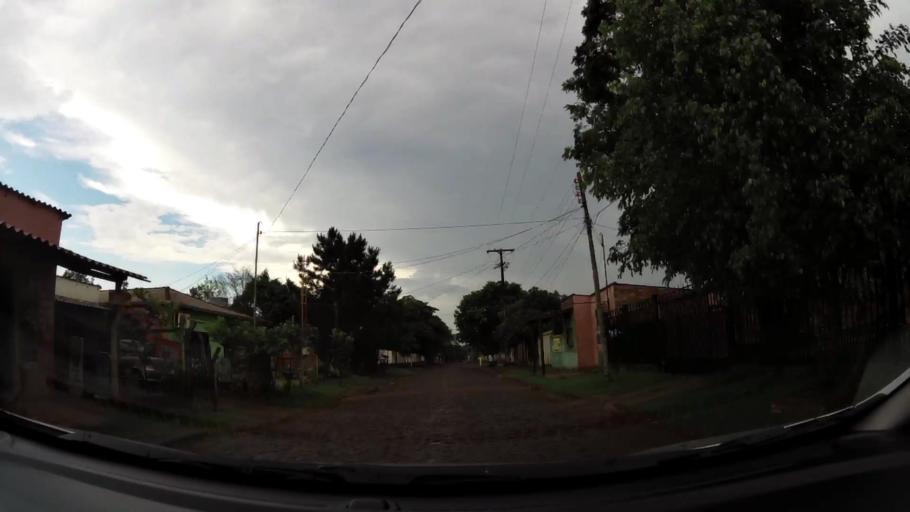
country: PY
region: Alto Parana
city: Presidente Franco
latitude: -25.5506
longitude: -54.6513
